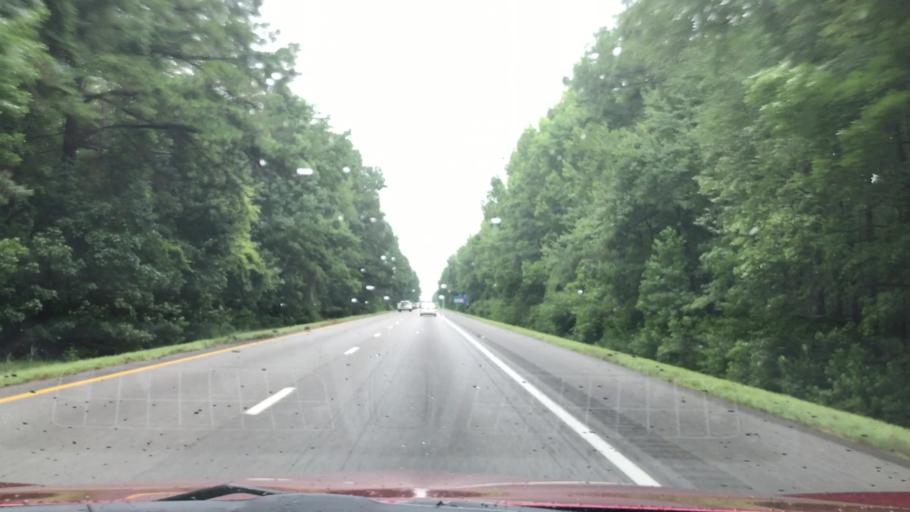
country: US
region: South Carolina
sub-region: Dorchester County
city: Ridgeville
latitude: 33.1423
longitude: -80.3216
